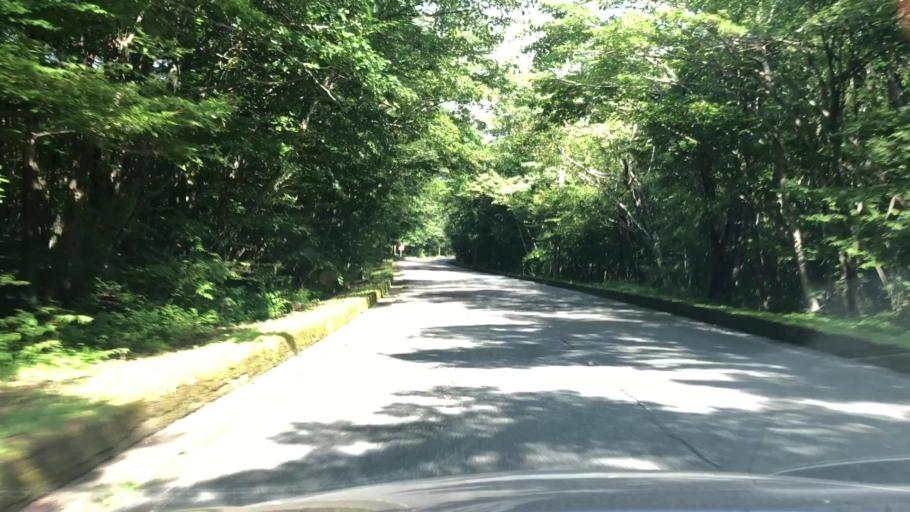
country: JP
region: Shizuoka
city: Gotemba
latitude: 35.3306
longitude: 138.8397
